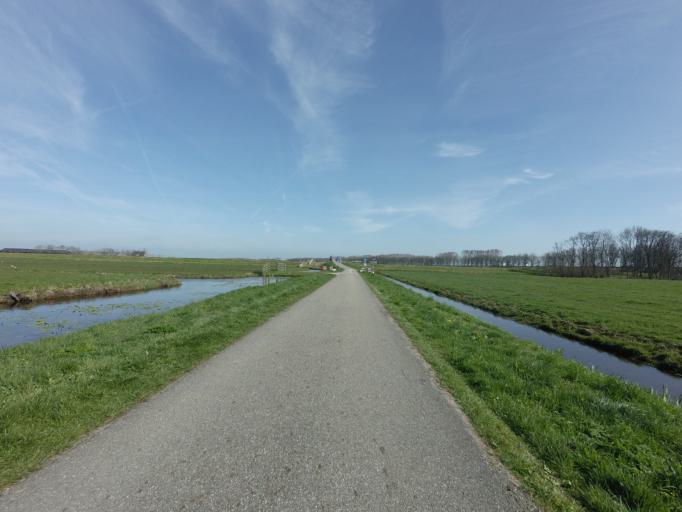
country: NL
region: South Holland
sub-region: Bodegraven-Reeuwijk
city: Bodegraven
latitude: 52.0666
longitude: 4.8047
